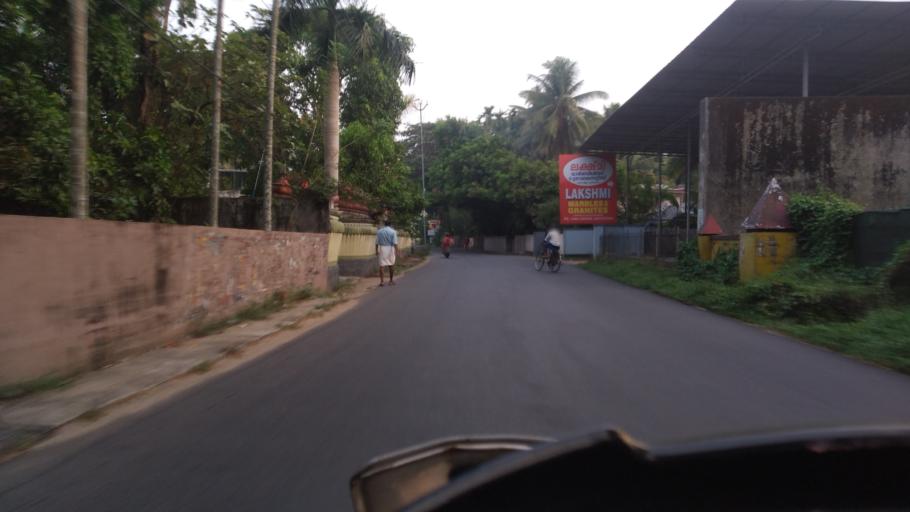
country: IN
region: Kerala
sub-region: Thrissur District
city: Kodungallur
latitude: 10.1840
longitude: 76.2046
